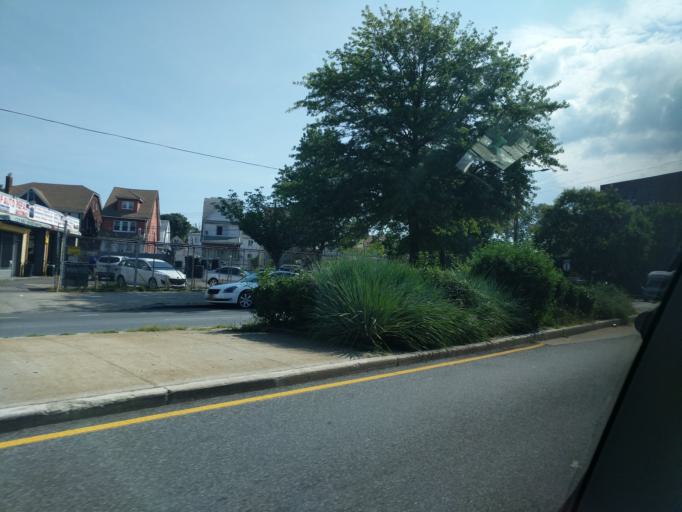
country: US
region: New York
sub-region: Queens County
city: Jamaica
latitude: 40.6977
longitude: -73.7853
